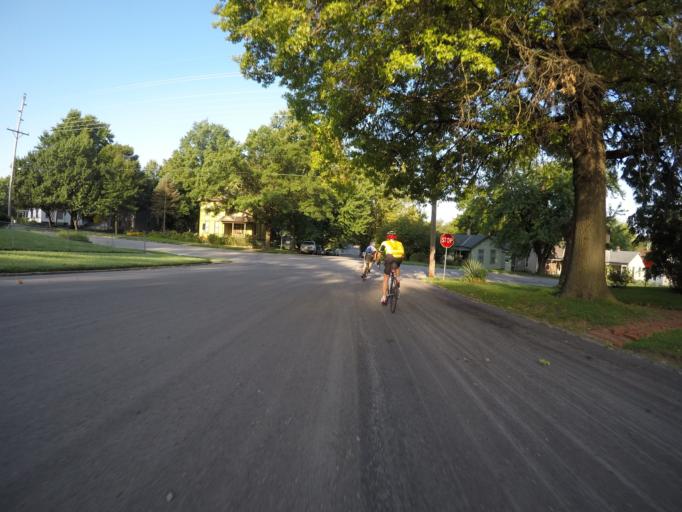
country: US
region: Kansas
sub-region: Leavenworth County
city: Leavenworth
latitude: 39.3124
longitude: -94.9090
